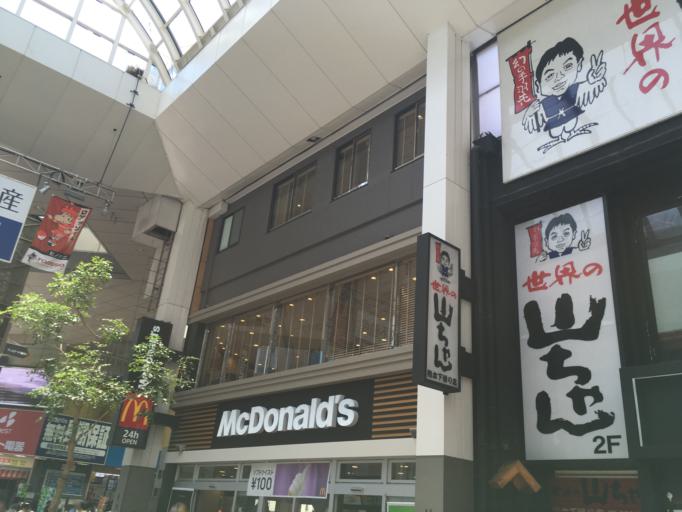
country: JP
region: Kumamoto
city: Kumamoto
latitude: 32.7992
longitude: 130.7077
